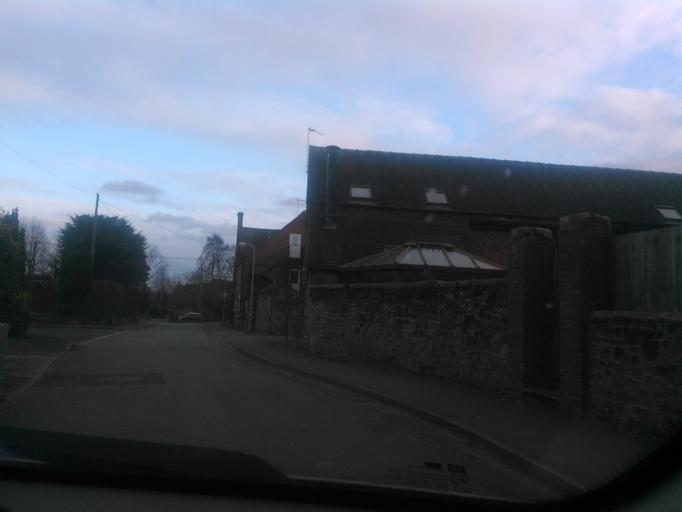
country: GB
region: England
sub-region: Telford and Wrekin
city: Chetwynd
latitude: 52.8343
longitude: -2.4578
